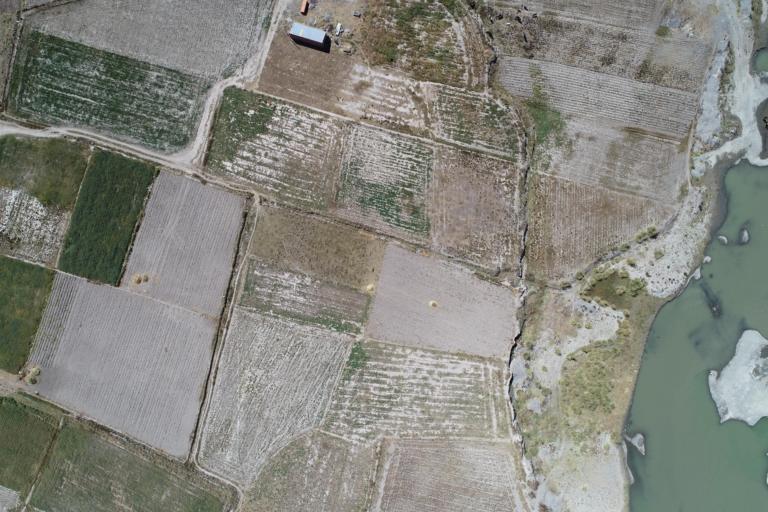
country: BO
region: La Paz
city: Achacachi
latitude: -16.0394
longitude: -68.6963
